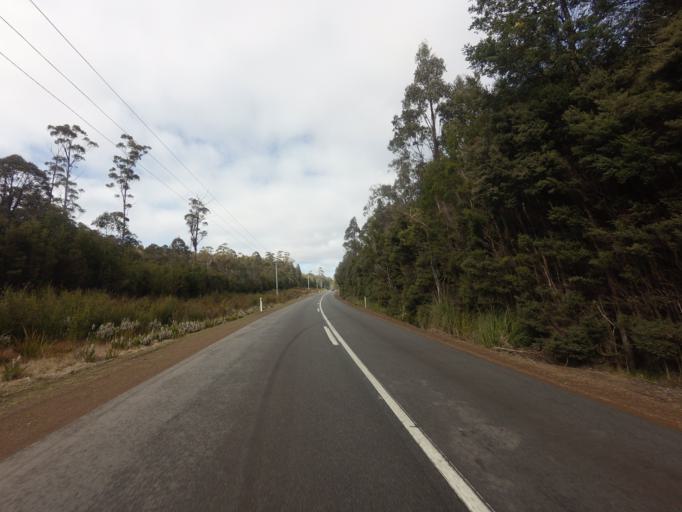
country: AU
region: Tasmania
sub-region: Huon Valley
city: Geeveston
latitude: -43.3666
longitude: 146.9589
